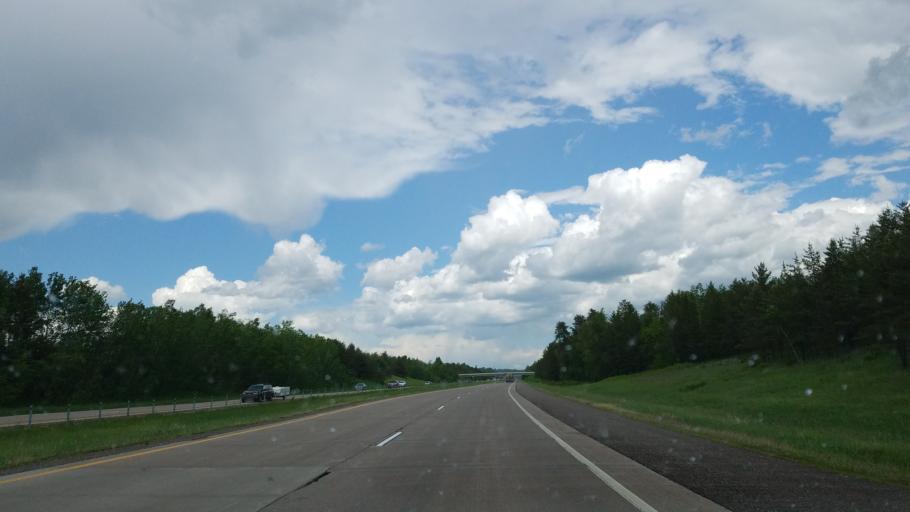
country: US
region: Minnesota
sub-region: Carlton County
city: Moose Lake
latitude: 46.4863
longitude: -92.7054
